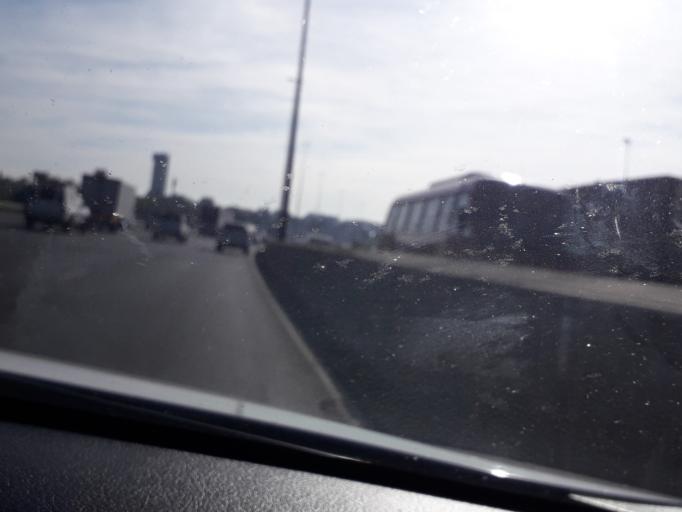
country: ZA
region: Gauteng
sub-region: Ekurhuleni Metropolitan Municipality
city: Germiston
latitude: -26.1645
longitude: 28.1476
